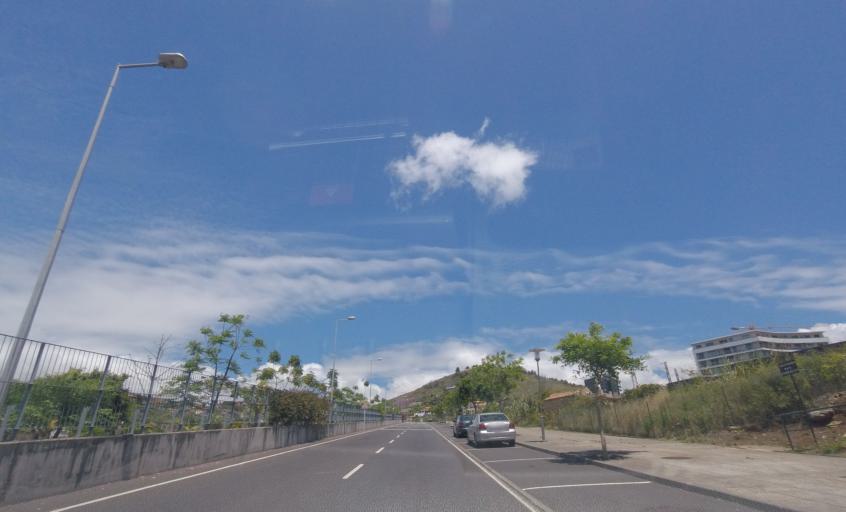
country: PT
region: Madeira
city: Camara de Lobos
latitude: 32.6435
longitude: -16.9455
